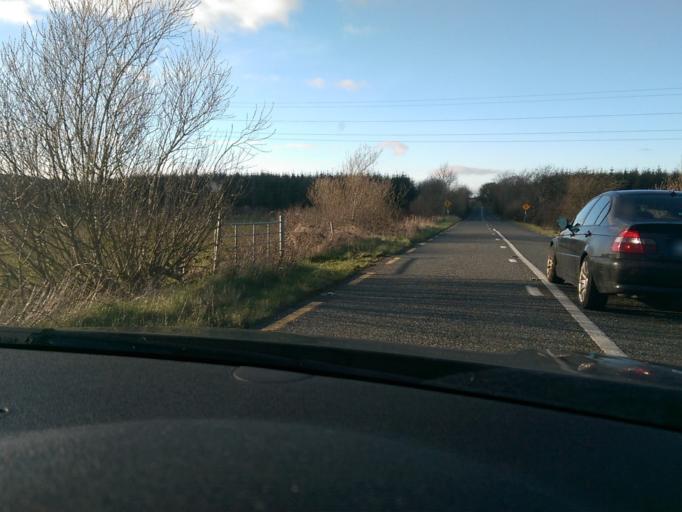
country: IE
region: Connaught
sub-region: Roscommon
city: Boyle
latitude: 53.9149
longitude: -8.2717
